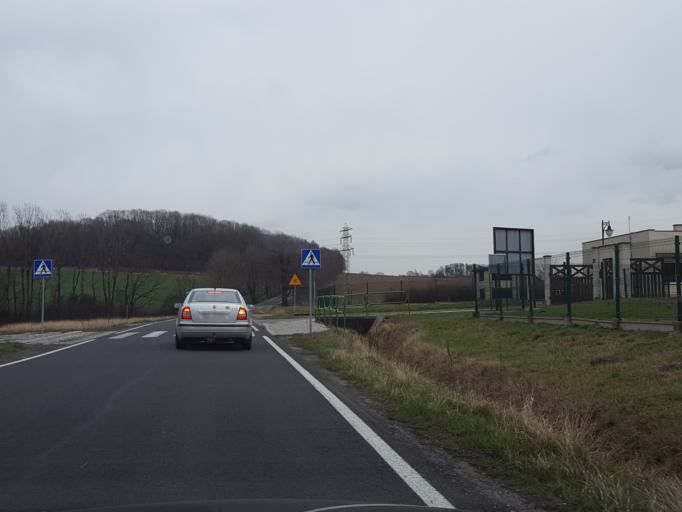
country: PL
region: Silesian Voivodeship
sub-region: Powiat mikolowski
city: Laziska Gorne
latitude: 50.1824
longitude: 18.8291
